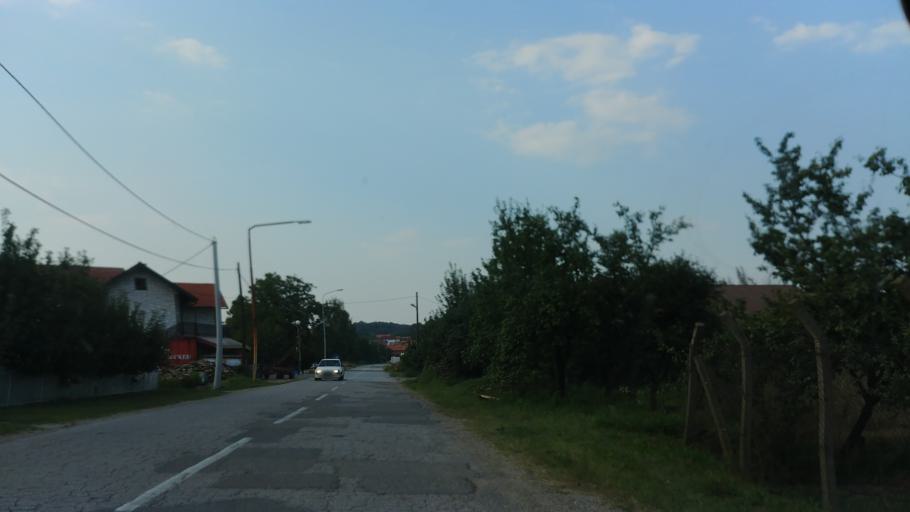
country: BA
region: Republika Srpska
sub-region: Opstina Ugljevik
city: Ugljevik
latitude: 44.6923
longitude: 19.0137
